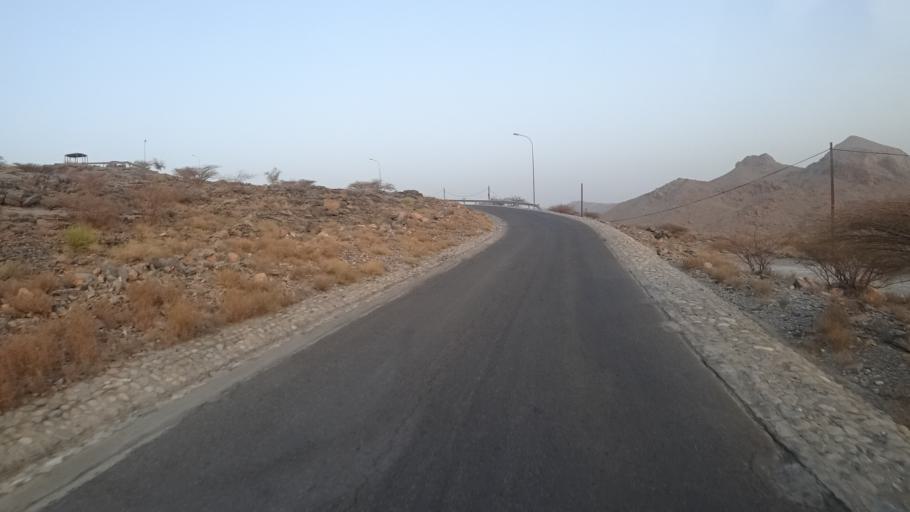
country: OM
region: Muhafazat ad Dakhiliyah
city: Bahla'
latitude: 23.1286
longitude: 57.2970
